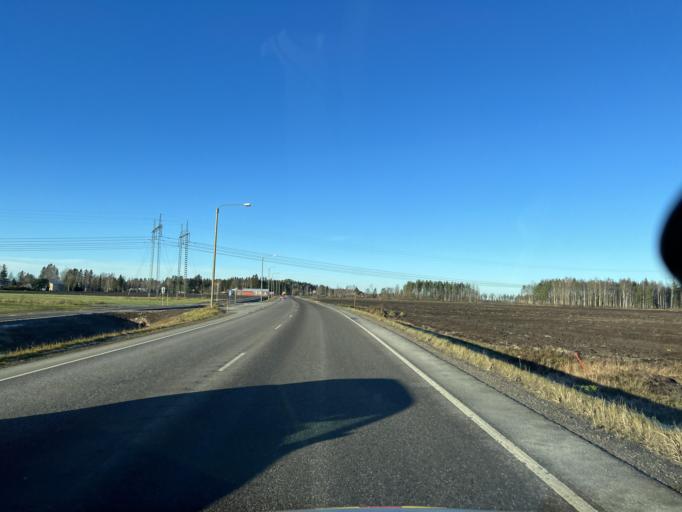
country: FI
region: Northern Ostrobothnia
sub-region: Nivala-Haapajaervi
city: Nivala
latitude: 63.9530
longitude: 24.8729
